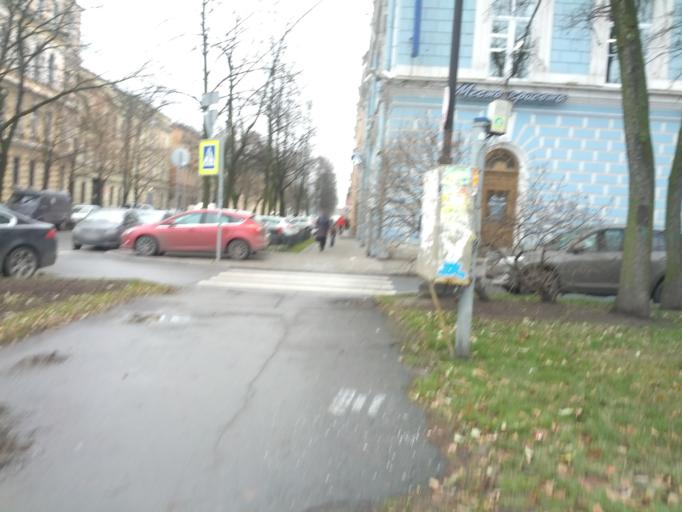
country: RU
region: St.-Petersburg
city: Vasyl'evsky Ostrov
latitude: 59.9368
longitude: 30.2755
